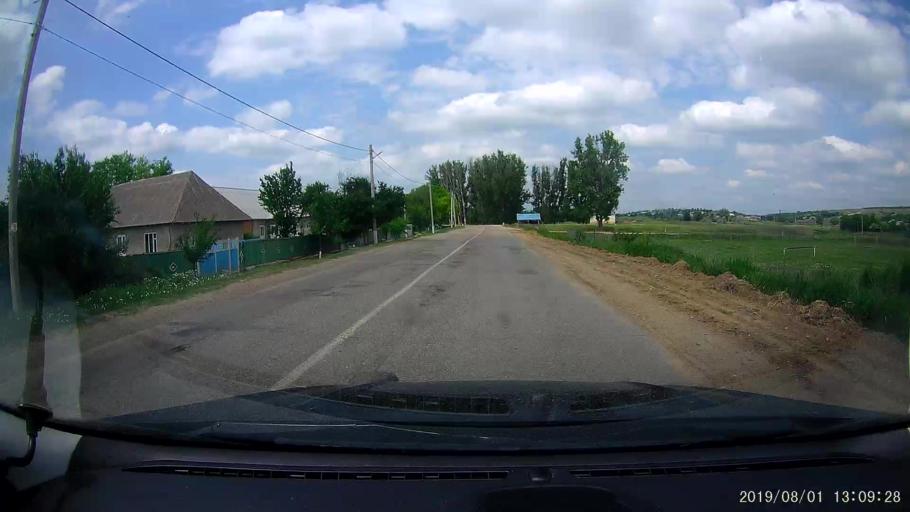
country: MD
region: Cahul
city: Cahul
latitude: 45.8269
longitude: 28.3177
